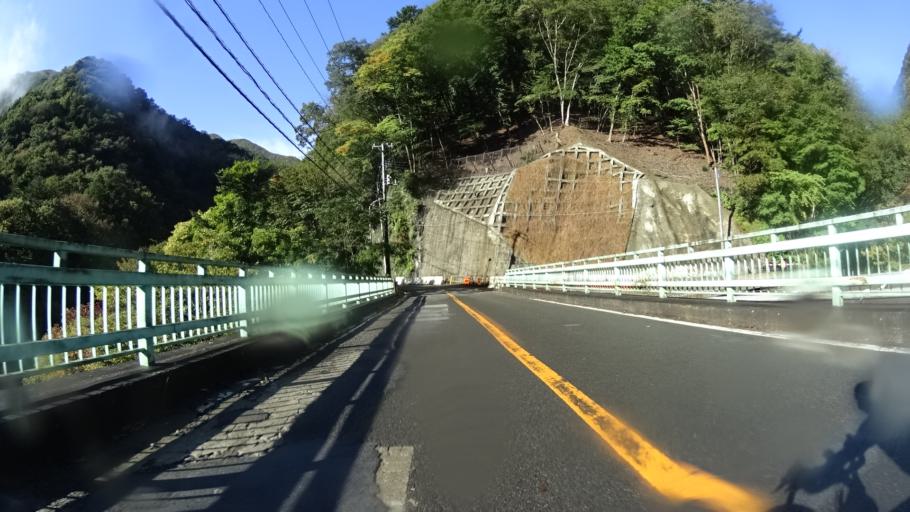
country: JP
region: Yamanashi
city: Otsuki
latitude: 35.7879
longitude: 138.9644
